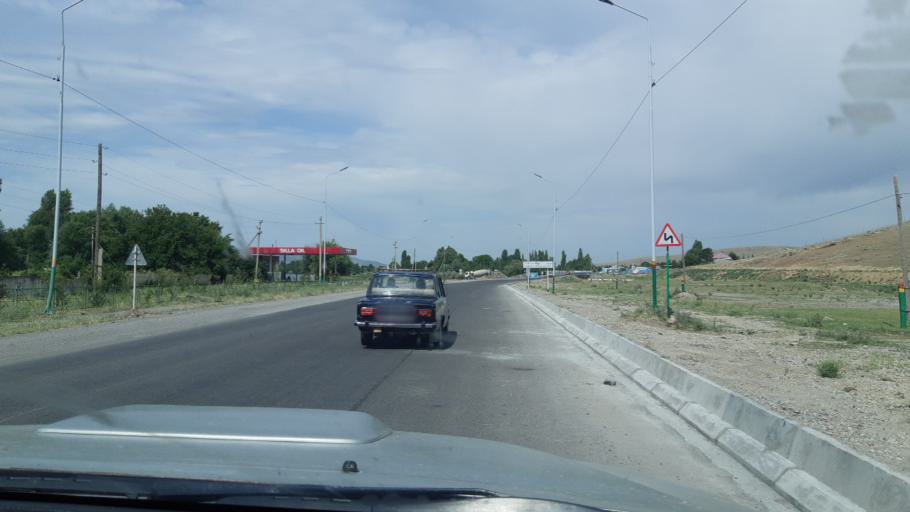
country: KZ
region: Ongtustik Qazaqstan
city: Turar Ryskulov
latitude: 42.5493
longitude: 70.3041
